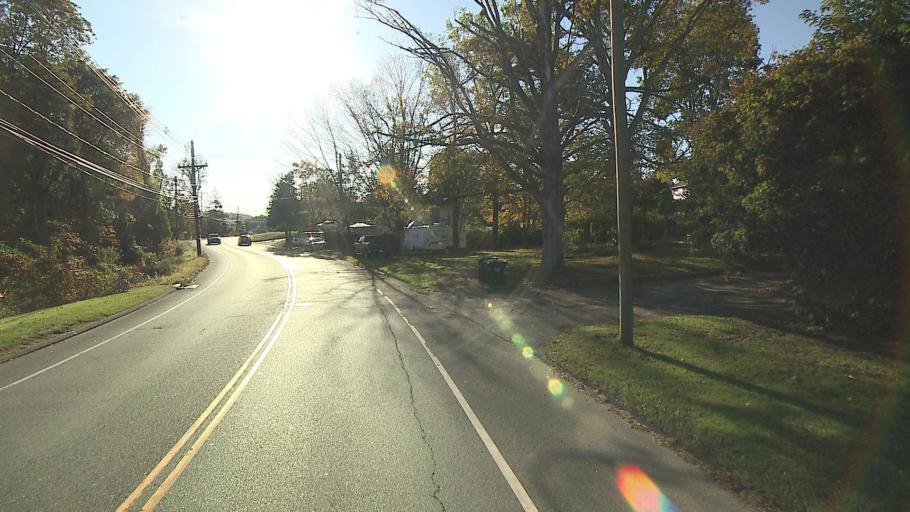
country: US
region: Connecticut
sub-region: Fairfield County
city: Bethel
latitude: 41.3865
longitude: -73.4307
